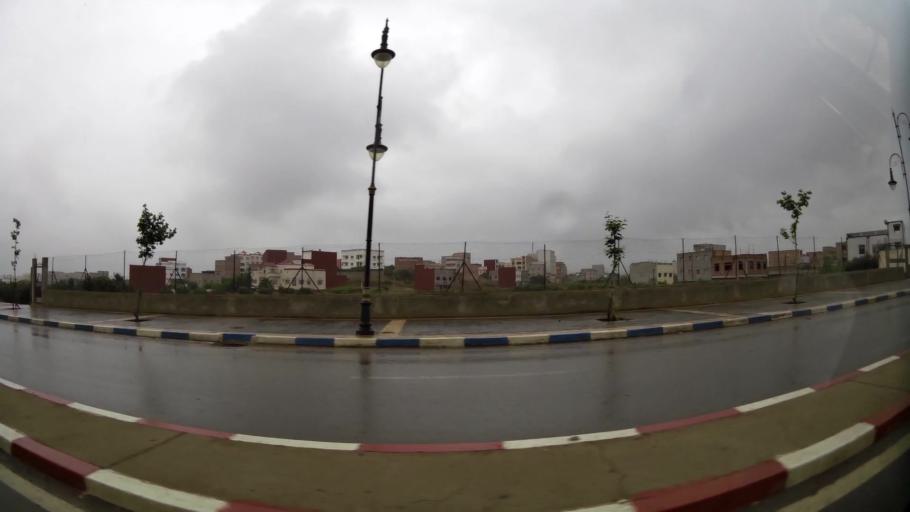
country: MA
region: Taza-Al Hoceima-Taounate
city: Imzourene
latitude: 35.1458
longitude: -3.8477
